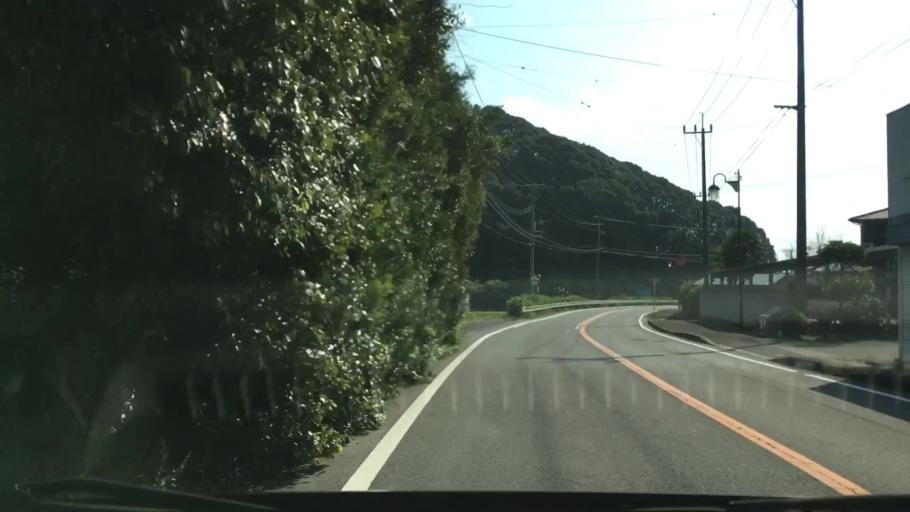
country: JP
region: Nagasaki
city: Togitsu
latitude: 32.9545
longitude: 129.7854
